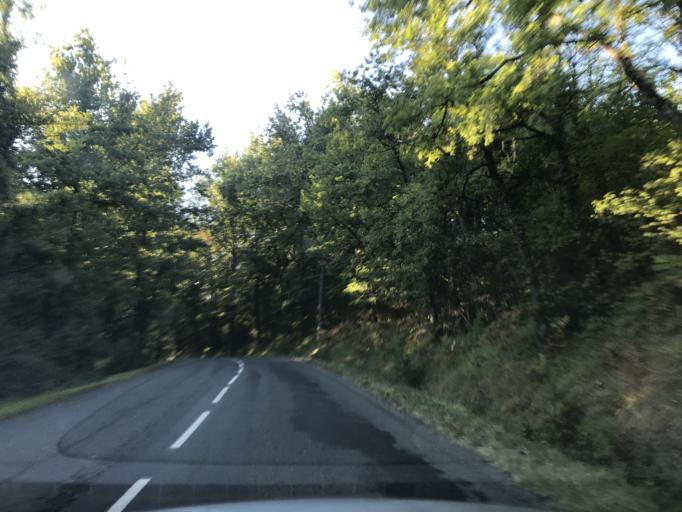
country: FR
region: Aquitaine
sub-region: Departement de la Gironde
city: Lussac
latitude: 44.9133
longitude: -0.0686
